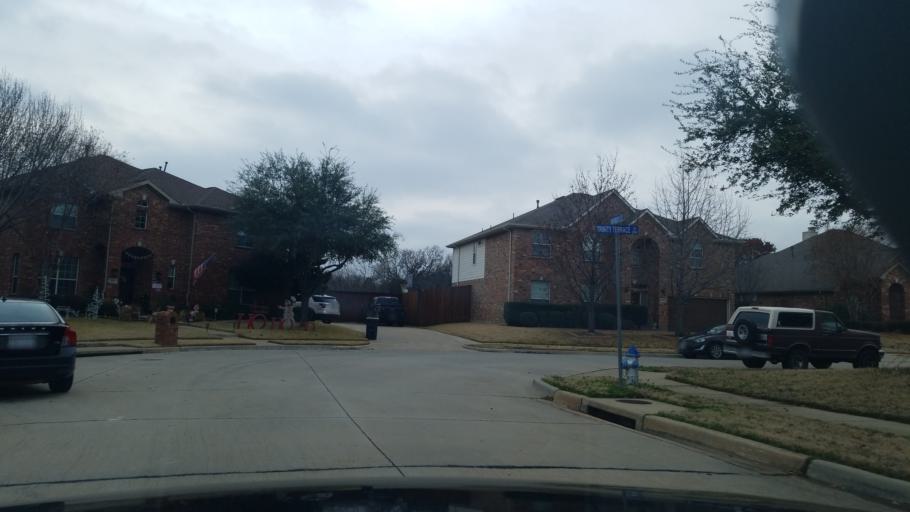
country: US
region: Texas
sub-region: Denton County
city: Corinth
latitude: 33.1406
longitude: -97.0672
